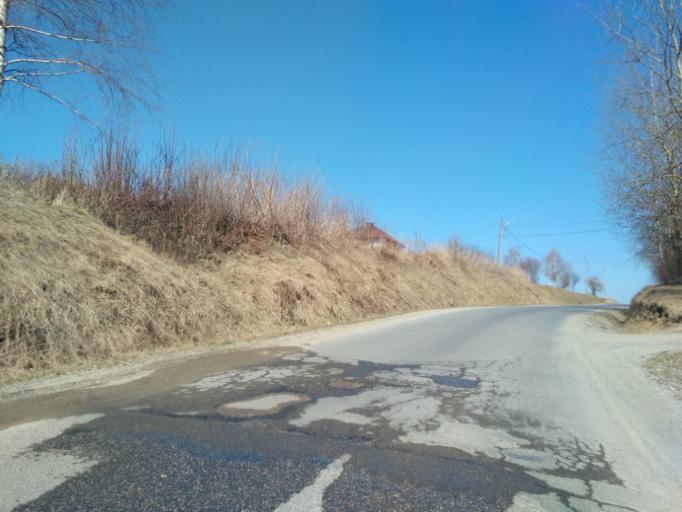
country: PL
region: Subcarpathian Voivodeship
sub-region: Powiat debicki
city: Brzostek
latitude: 49.9637
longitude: 21.4286
